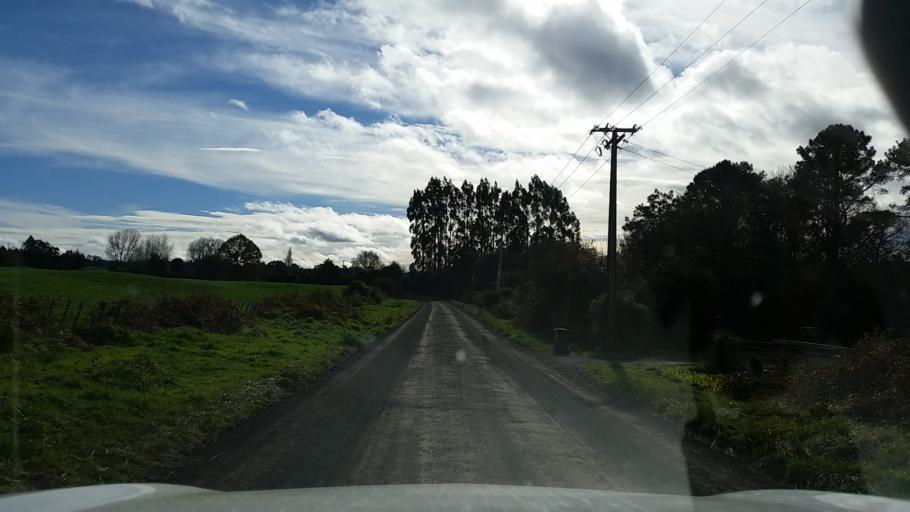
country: NZ
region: Bay of Plenty
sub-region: Rotorua District
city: Rotorua
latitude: -38.0641
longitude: 176.2099
